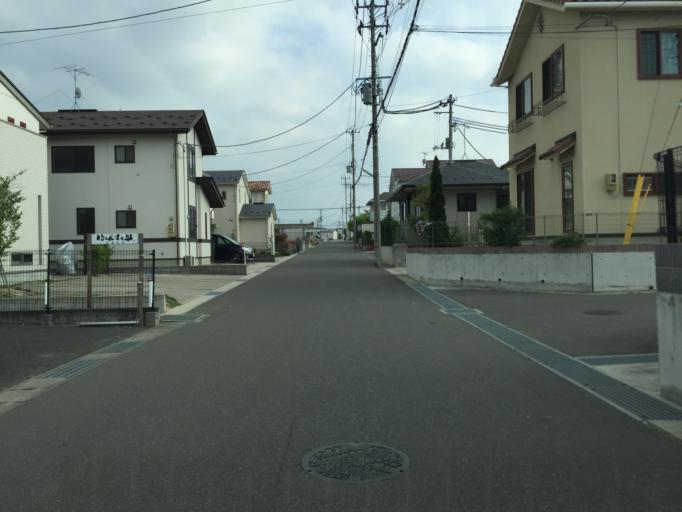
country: JP
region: Fukushima
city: Fukushima-shi
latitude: 37.7319
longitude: 140.4502
